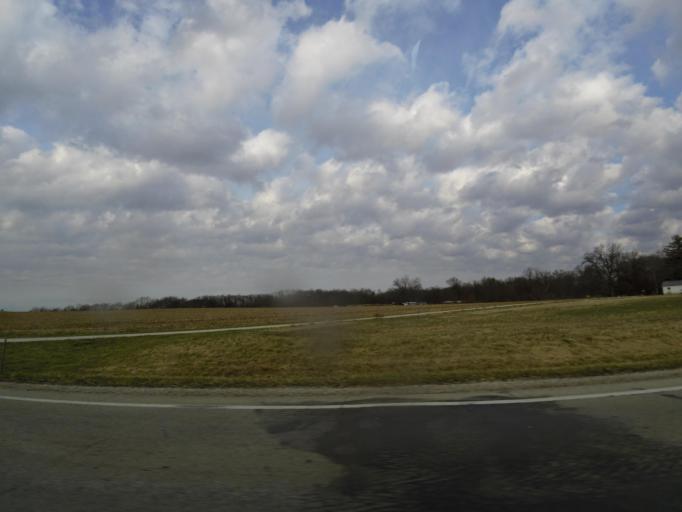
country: US
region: Illinois
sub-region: Christian County
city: Pana
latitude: 39.2997
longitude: -89.0905
